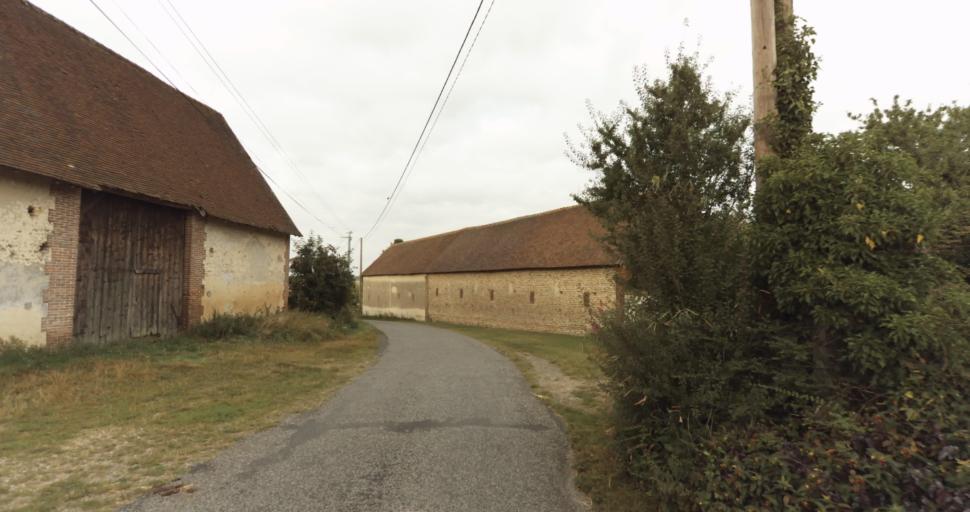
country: FR
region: Centre
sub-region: Departement d'Eure-et-Loir
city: Vert-en-Drouais
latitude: 48.7959
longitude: 1.2881
